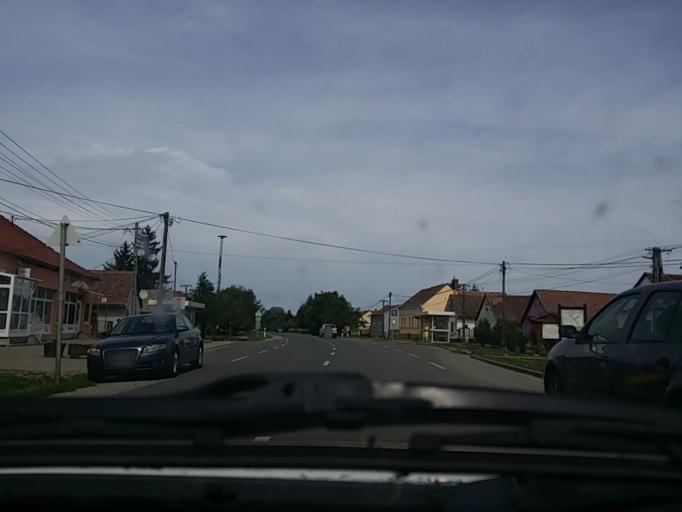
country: HR
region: Osjecko-Baranjska
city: Viljevo
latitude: 45.8246
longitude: 18.1016
